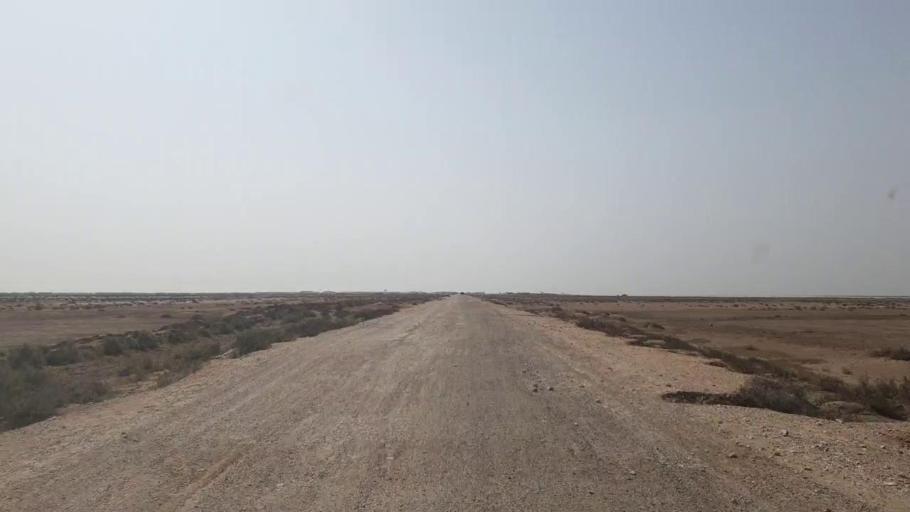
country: PK
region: Sindh
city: Jati
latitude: 24.3520
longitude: 68.5937
